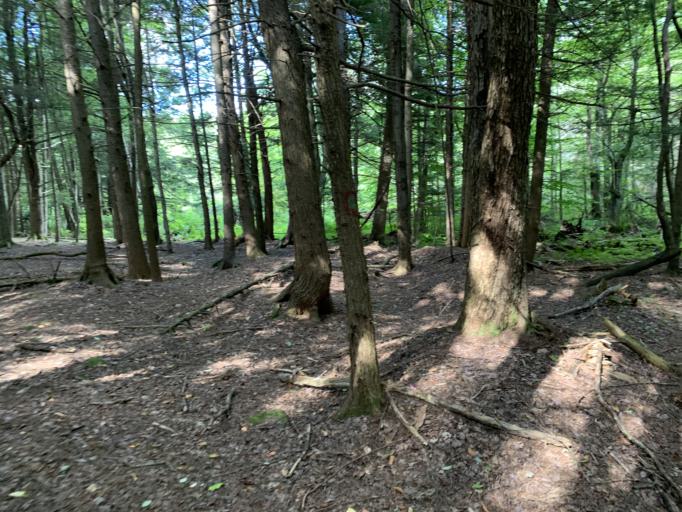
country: US
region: Massachusetts
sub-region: Berkshire County
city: Becket
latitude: 42.2970
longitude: -73.0626
